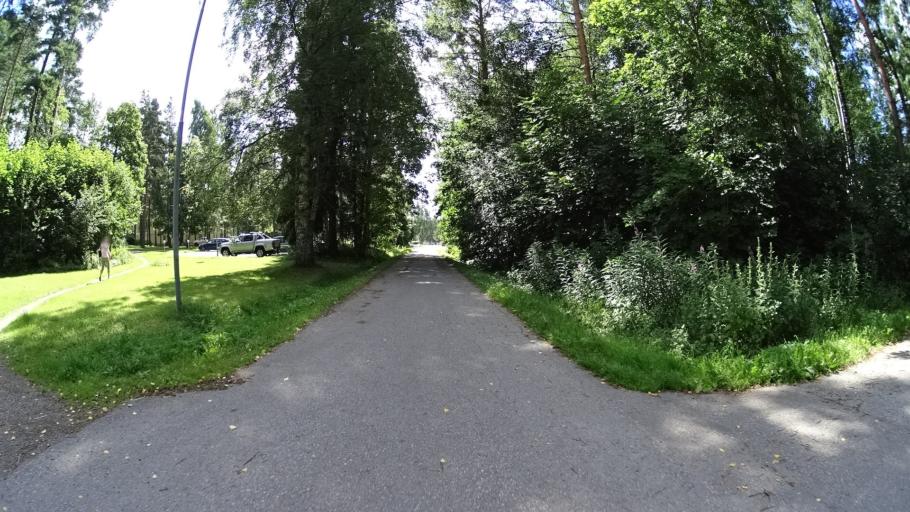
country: FI
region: Uusimaa
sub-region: Helsinki
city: Tuusula
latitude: 60.3915
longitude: 25.0251
